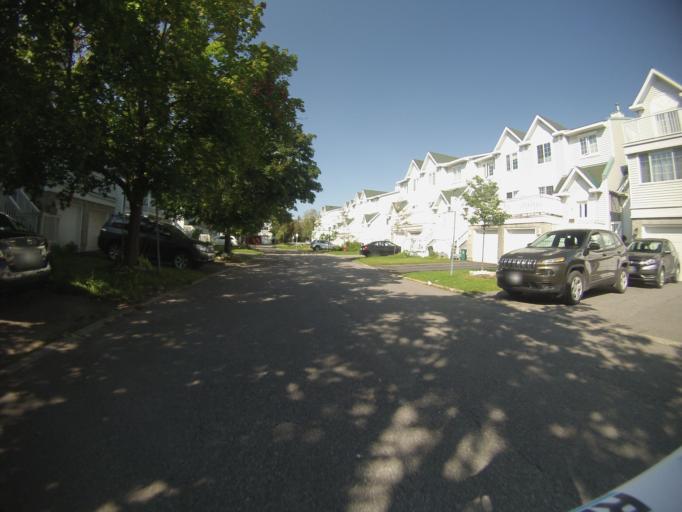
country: CA
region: Ontario
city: Ottawa
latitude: 45.3637
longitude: -75.6299
